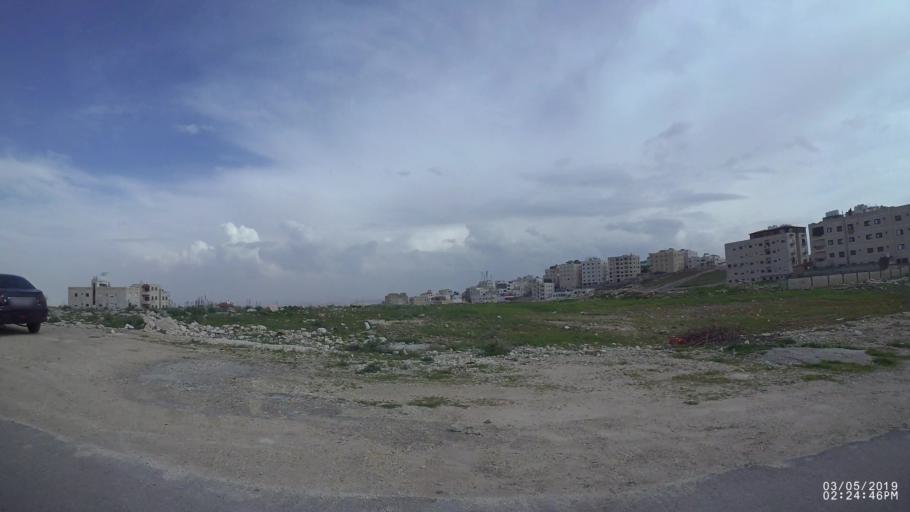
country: JO
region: Amman
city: Amman
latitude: 32.0160
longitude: 35.9403
